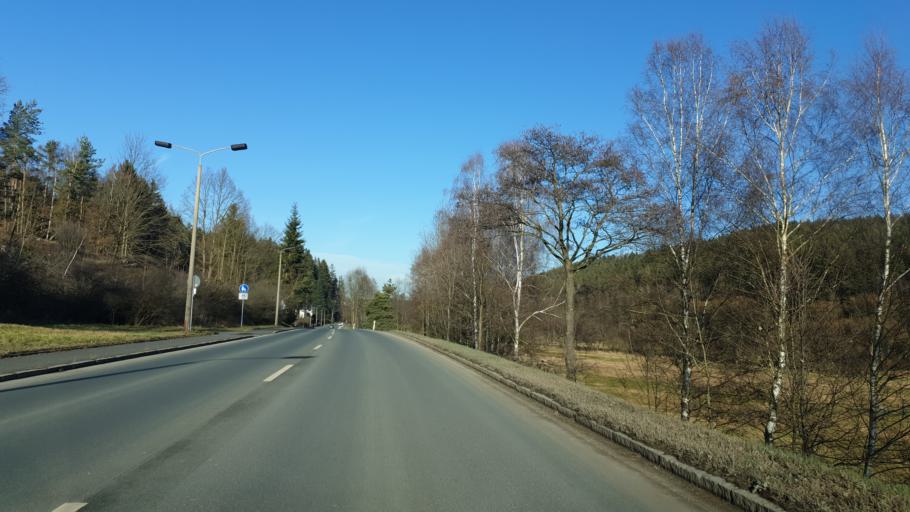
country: DE
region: Saxony
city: Adorf
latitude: 50.3026
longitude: 12.2530
